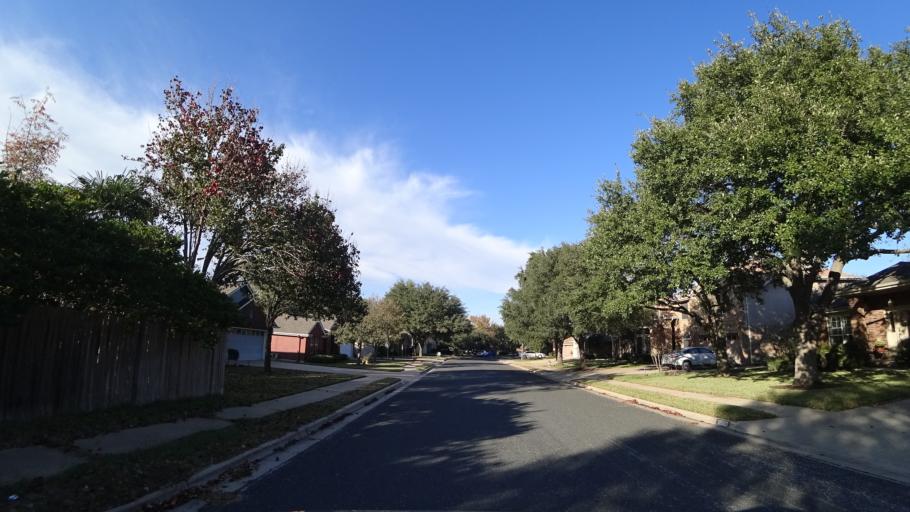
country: US
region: Texas
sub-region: Williamson County
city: Brushy Creek
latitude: 30.5037
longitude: -97.7416
